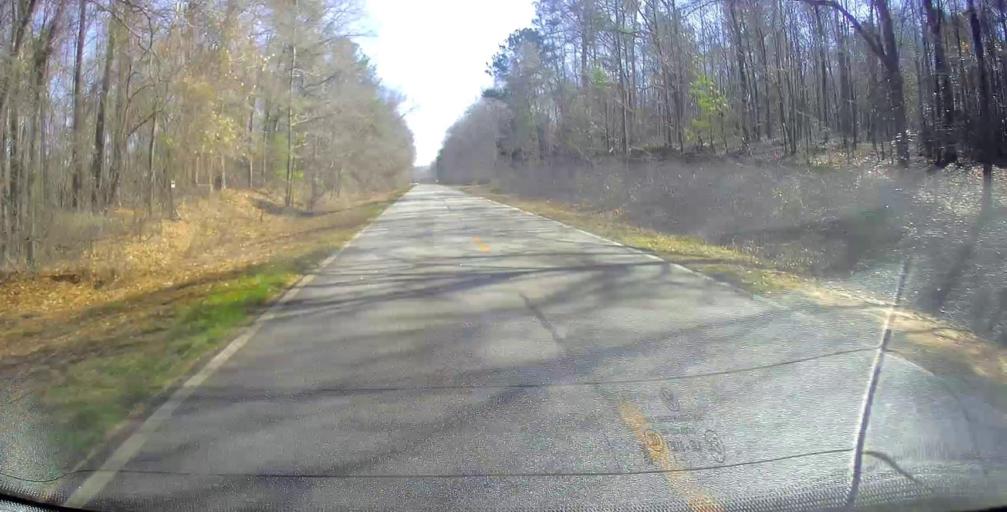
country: US
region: Georgia
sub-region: Peach County
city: Byron
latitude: 32.6054
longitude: -83.8011
